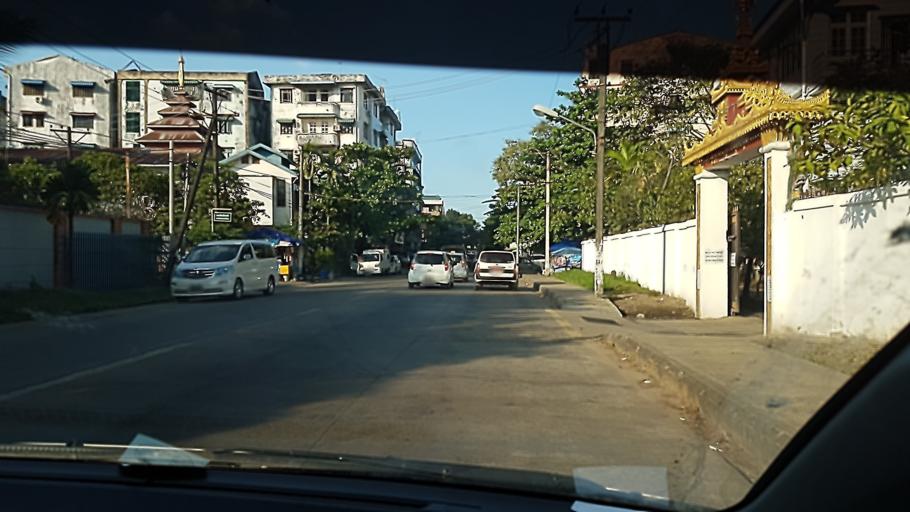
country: MM
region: Yangon
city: Yangon
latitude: 16.8192
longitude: 96.1759
